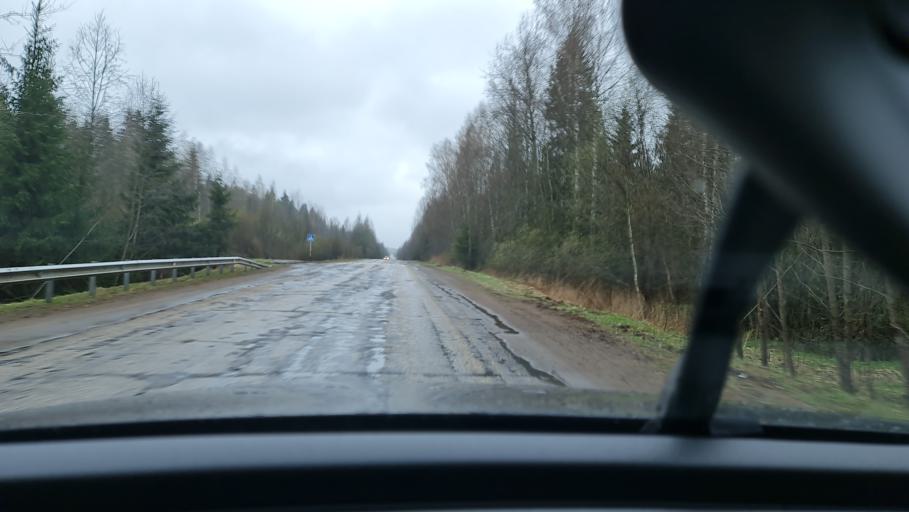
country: RU
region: Novgorod
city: Valday
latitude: 58.0355
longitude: 32.8719
